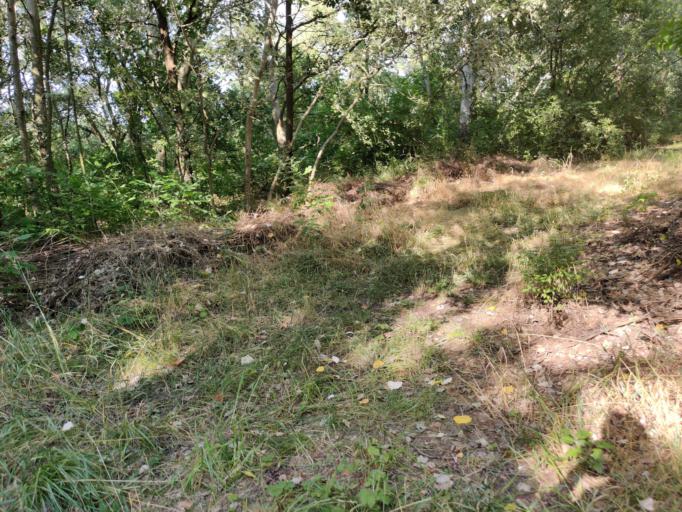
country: HU
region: Hajdu-Bihar
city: Balmazujvaros
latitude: 47.6166
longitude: 21.3324
